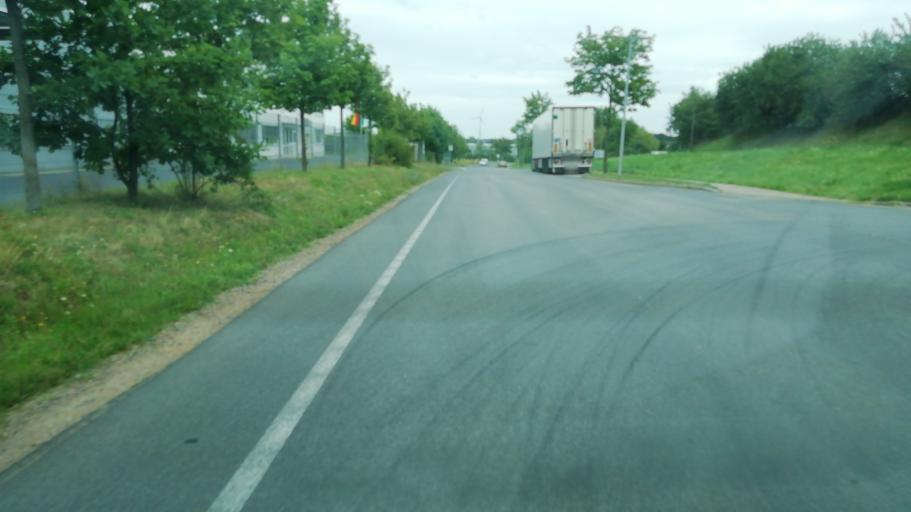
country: DE
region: Saxony
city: Wilsdruff
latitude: 51.0603
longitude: 13.5515
